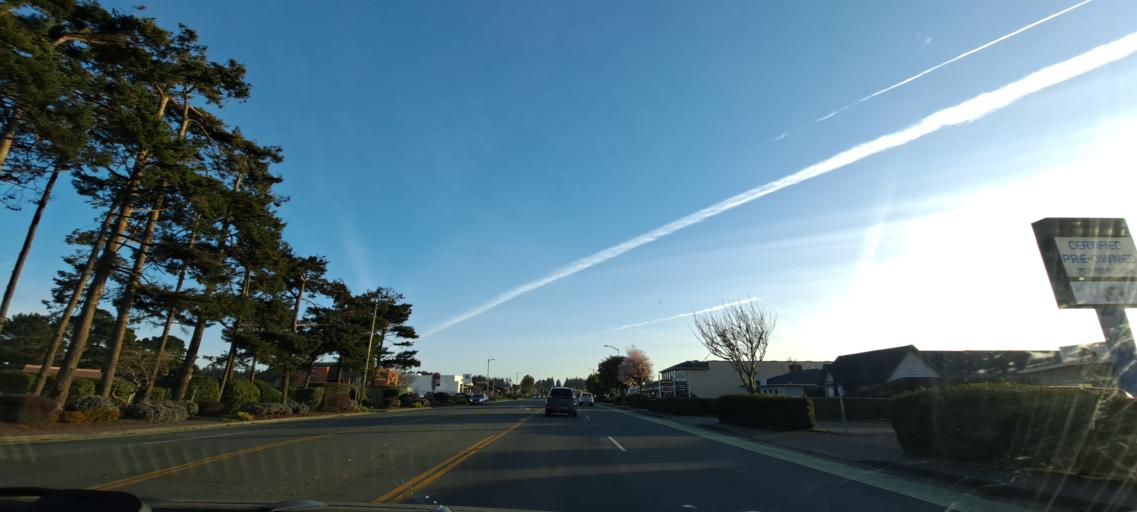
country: US
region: California
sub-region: Humboldt County
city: McKinleyville
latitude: 40.9389
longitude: -124.1009
